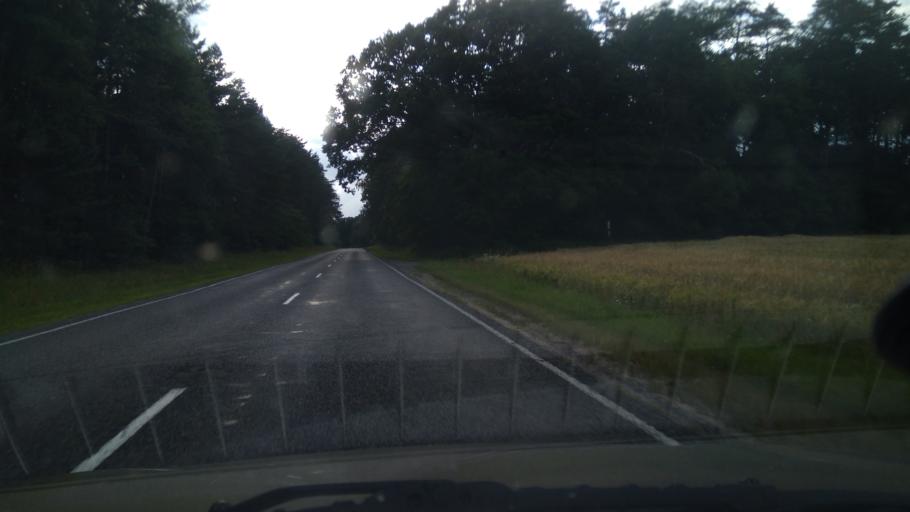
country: BY
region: Grodnenskaya
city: Masty
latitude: 53.3467
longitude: 24.6591
